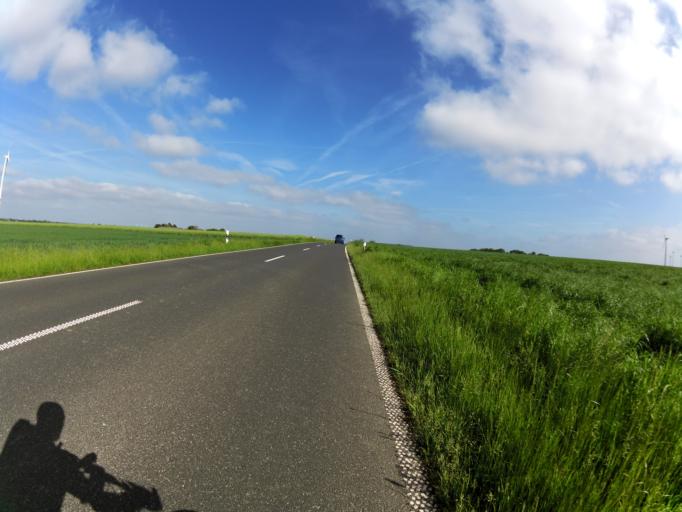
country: DE
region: North Rhine-Westphalia
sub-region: Regierungsbezirk Koln
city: Linnich
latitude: 50.9777
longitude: 6.2162
